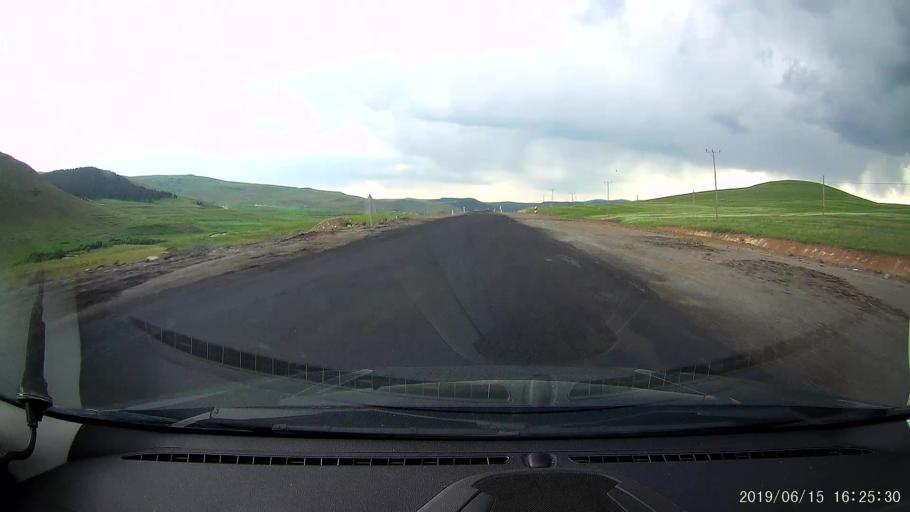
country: TR
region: Ardahan
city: Hanak
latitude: 41.1530
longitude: 42.8690
